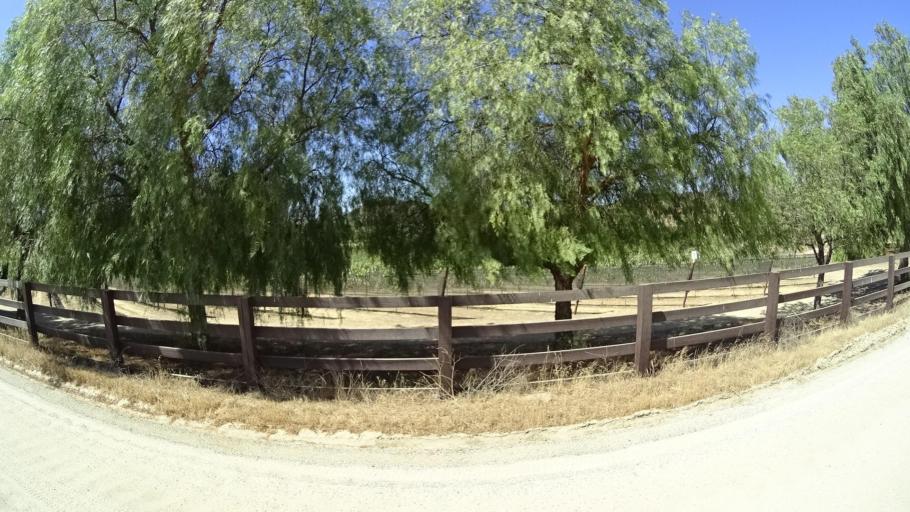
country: US
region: California
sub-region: San Diego County
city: San Diego Country Estates
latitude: 33.0599
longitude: -116.7518
